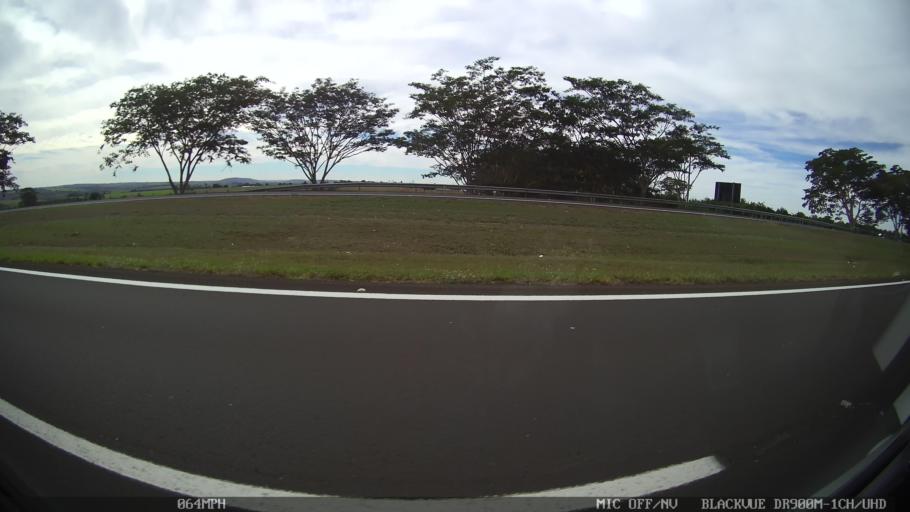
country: BR
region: Sao Paulo
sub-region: Taquaritinga
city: Taquaritinga
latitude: -21.4685
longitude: -48.6092
